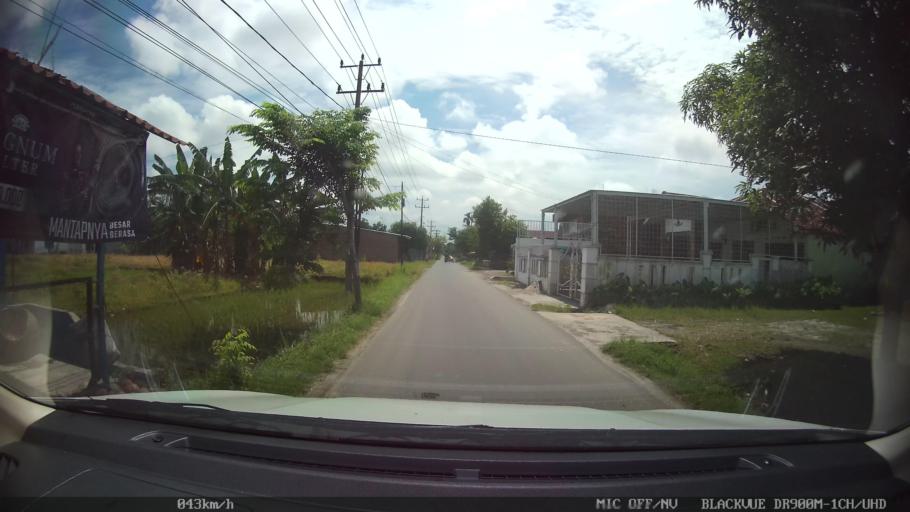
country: ID
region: North Sumatra
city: Percut
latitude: 3.6019
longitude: 98.7851
